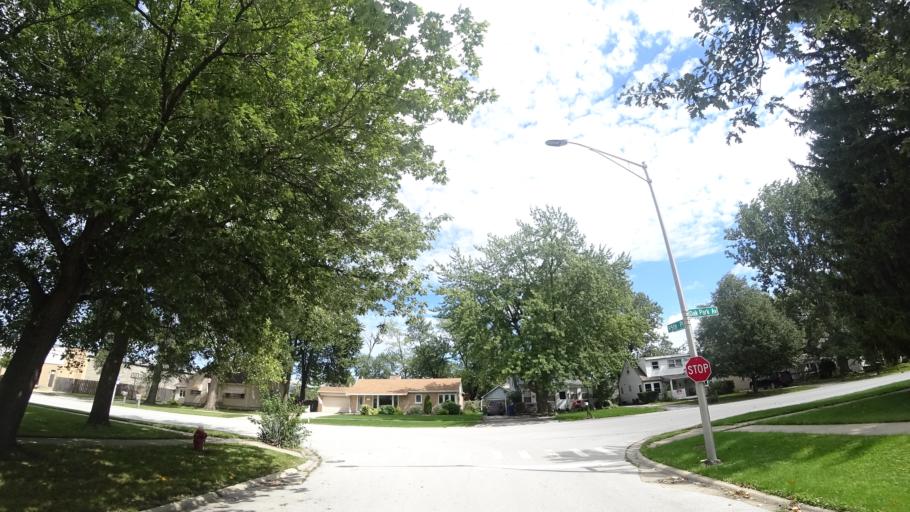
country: US
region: Illinois
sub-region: Cook County
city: Burbank
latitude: 41.7185
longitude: -87.7899
